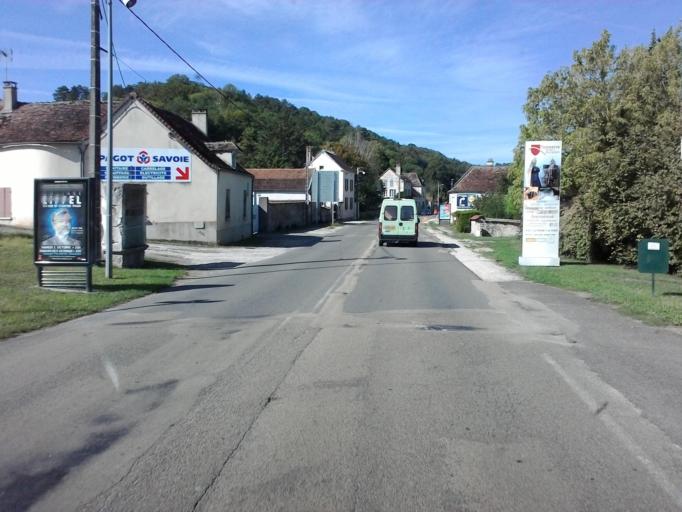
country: FR
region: Bourgogne
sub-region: Departement de l'Yonne
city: Tonnerre
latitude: 47.8513
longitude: 3.9887
